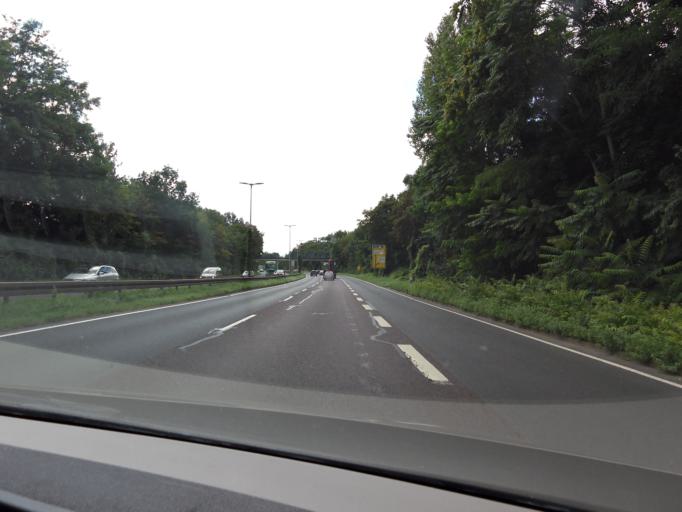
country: DE
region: Saxony-Anhalt
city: Magdeburg
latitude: 52.1274
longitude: 11.6199
